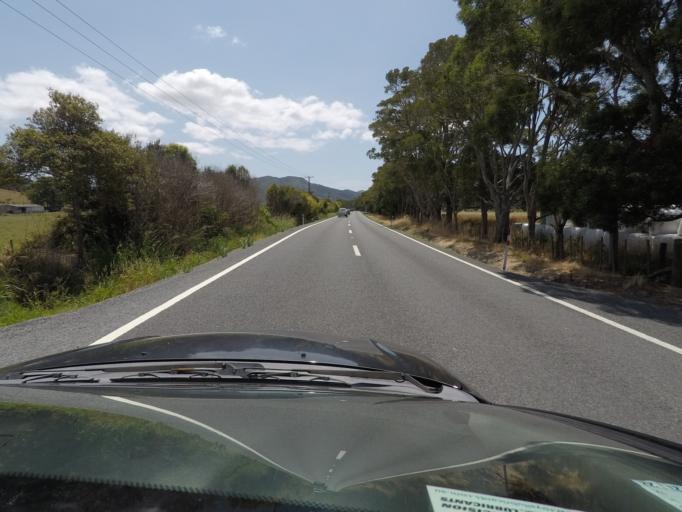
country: NZ
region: Auckland
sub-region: Auckland
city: Warkworth
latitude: -36.3352
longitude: 174.7343
